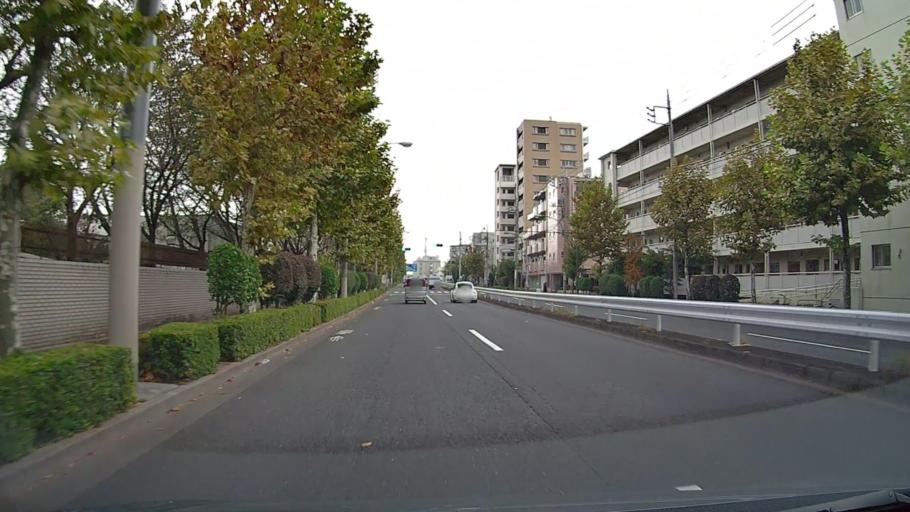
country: JP
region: Saitama
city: Wako
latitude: 35.7611
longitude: 139.6588
